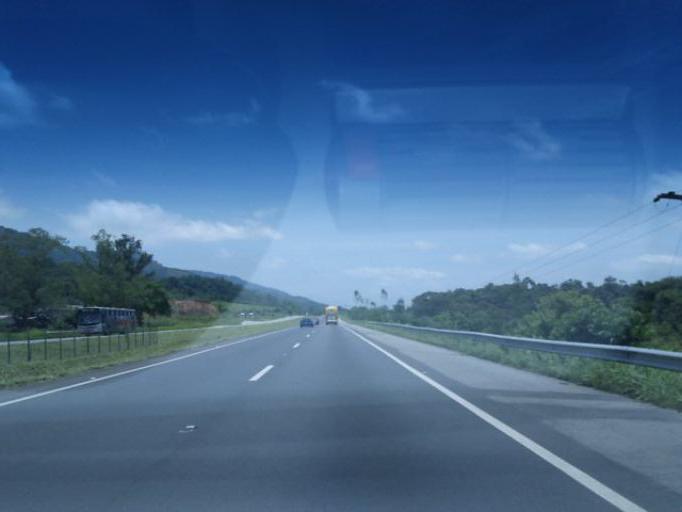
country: BR
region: Sao Paulo
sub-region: Miracatu
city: Miracatu
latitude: -24.2767
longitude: -47.4163
